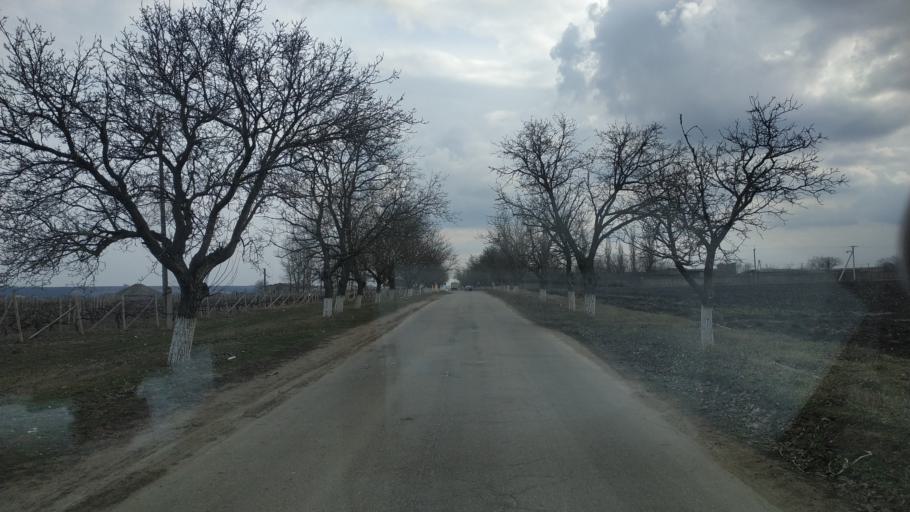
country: MD
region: Anenii Noi
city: Varnita
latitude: 46.8537
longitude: 29.3499
